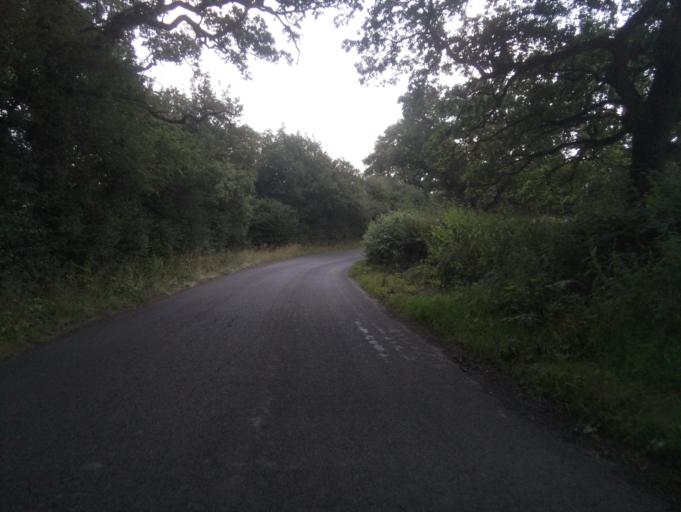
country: GB
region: England
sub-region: Wiltshire
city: Hankerton
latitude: 51.5804
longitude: -2.0100
